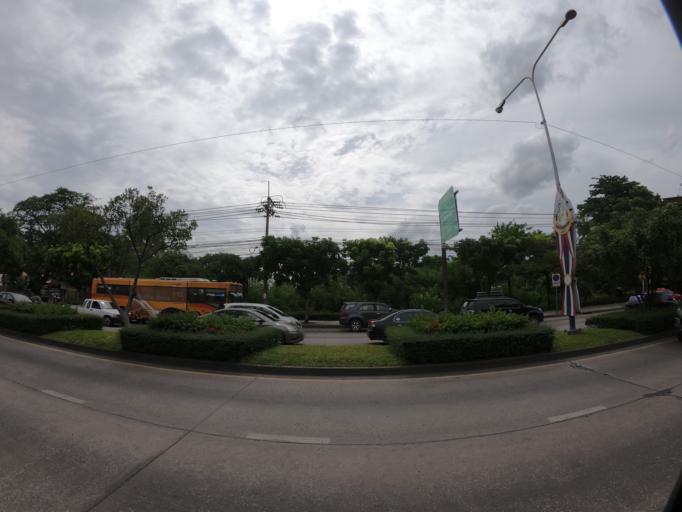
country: TH
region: Bangkok
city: Khan Na Yao
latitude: 13.8168
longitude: 100.6532
